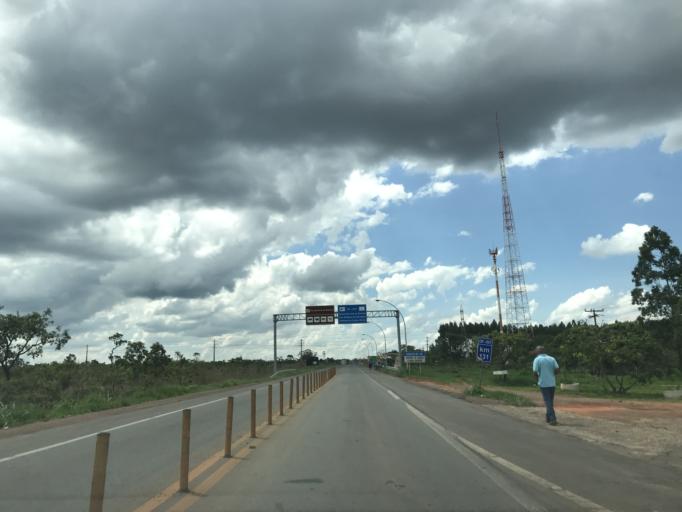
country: BR
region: Federal District
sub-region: Brasilia
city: Brasilia
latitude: -15.6866
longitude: -47.8616
